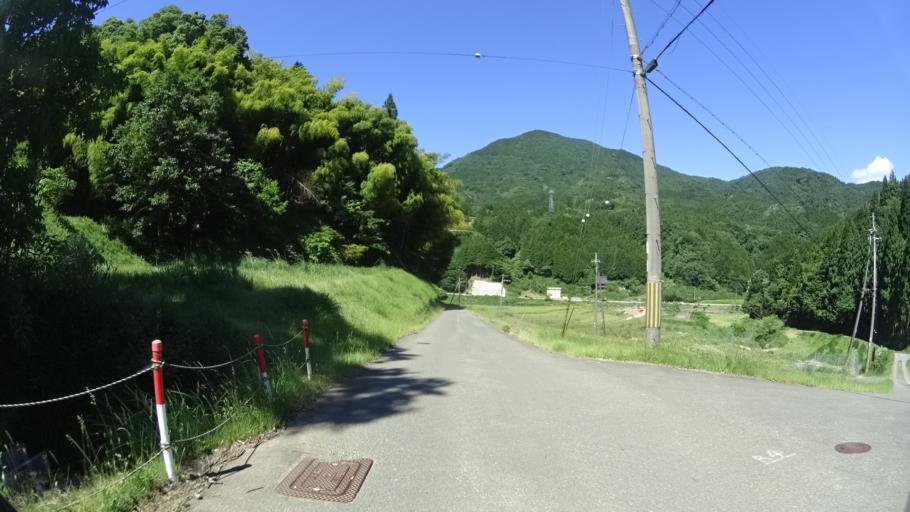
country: JP
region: Kyoto
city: Fukuchiyama
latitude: 35.3859
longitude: 135.0396
